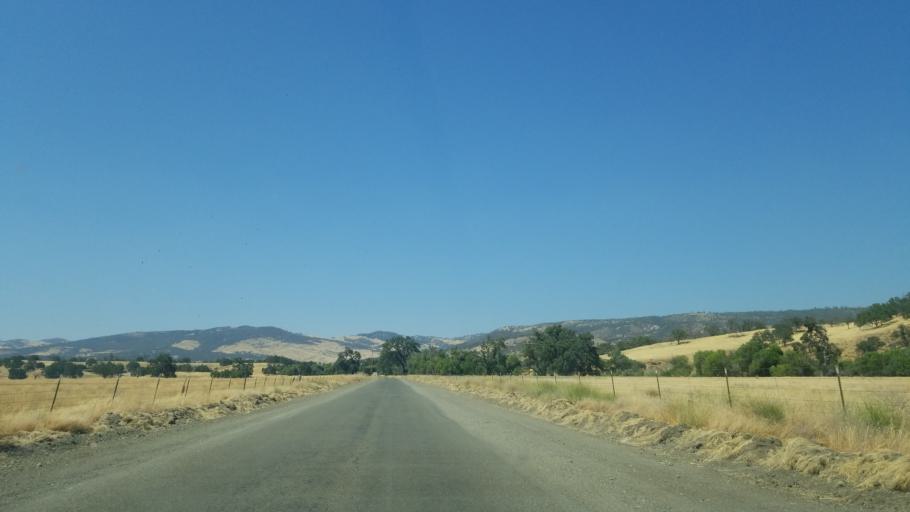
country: US
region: California
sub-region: San Luis Obispo County
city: Shandon
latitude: 35.8892
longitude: -120.4367
